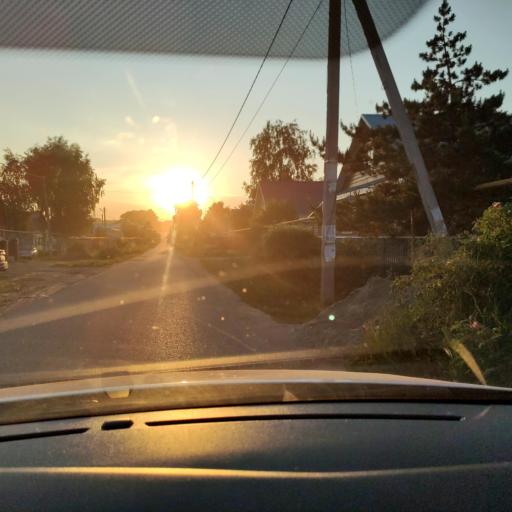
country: RU
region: Tatarstan
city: Stolbishchi
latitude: 55.7476
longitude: 49.3042
